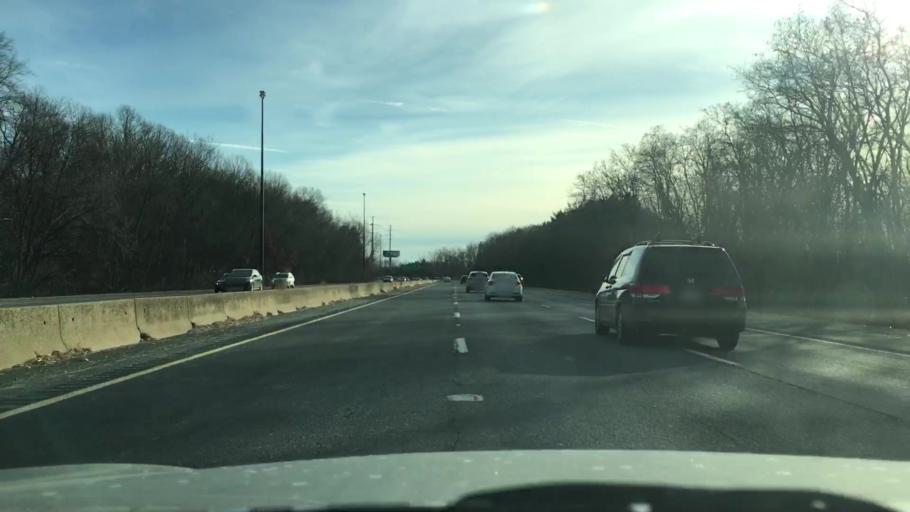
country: US
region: Massachusetts
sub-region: Hampden County
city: Chicopee
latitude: 42.1659
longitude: -72.6111
